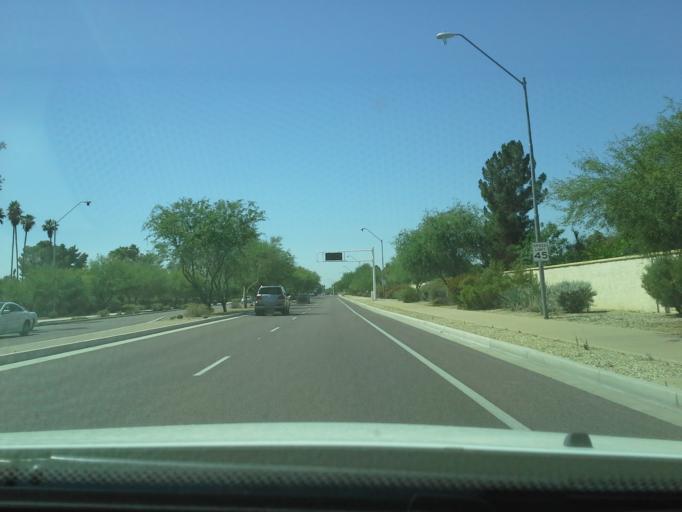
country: US
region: Arizona
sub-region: Maricopa County
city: Paradise Valley
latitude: 33.6005
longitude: -111.9087
